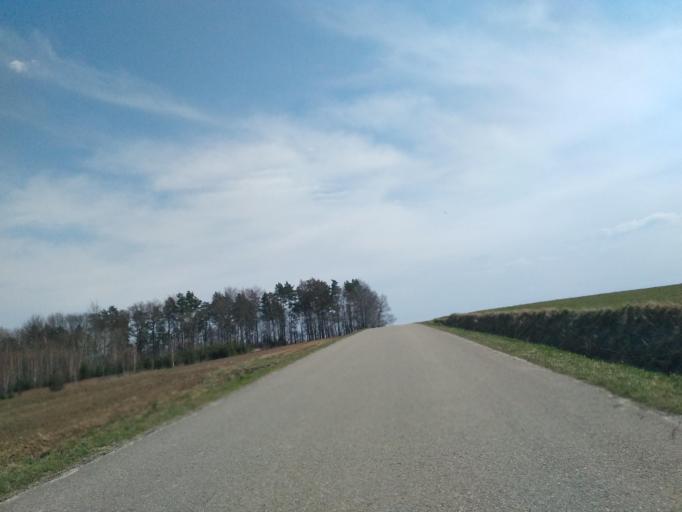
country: PL
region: Subcarpathian Voivodeship
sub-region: Powiat ropczycko-sedziszowski
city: Iwierzyce
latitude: 49.9726
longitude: 21.7529
